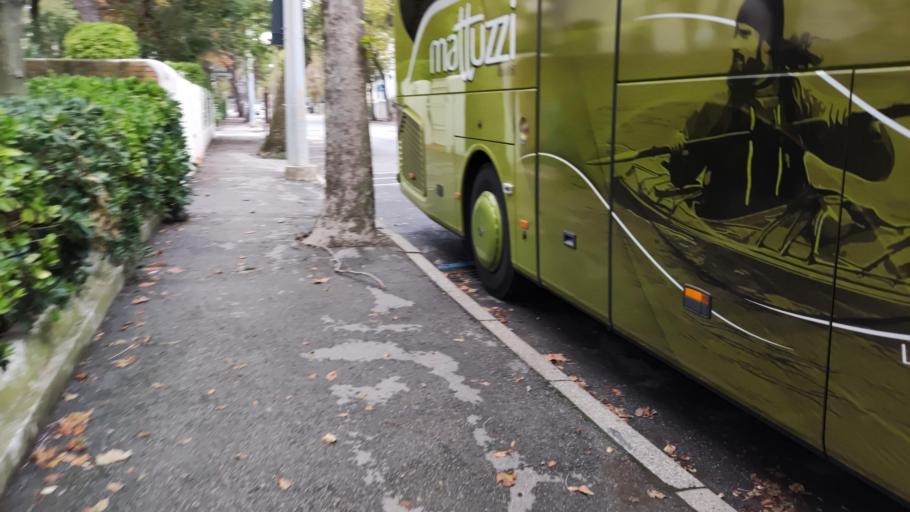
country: IT
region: Emilia-Romagna
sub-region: Provincia di Rimini
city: Riccione
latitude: 44.0080
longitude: 12.6531
